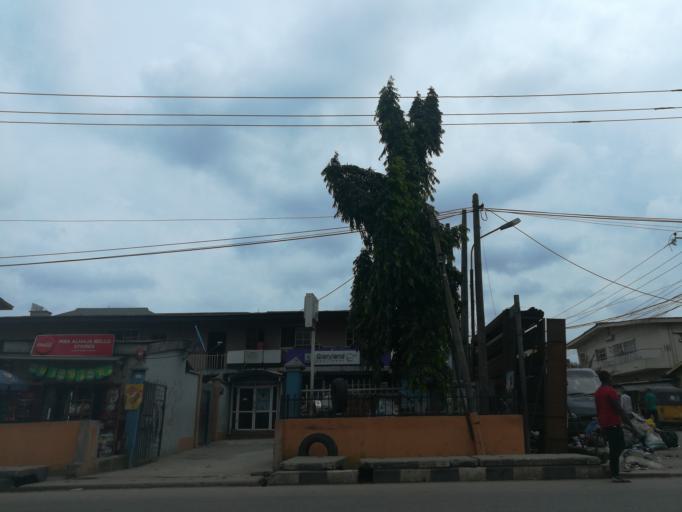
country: NG
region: Lagos
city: Ikeja
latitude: 6.6087
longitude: 3.3561
